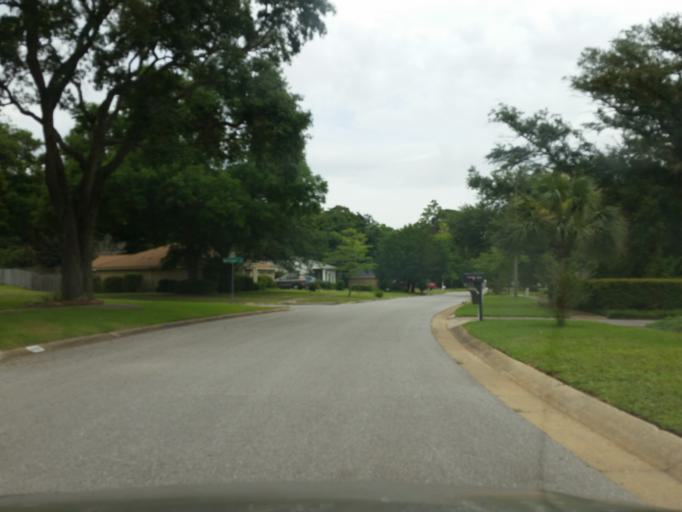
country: US
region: Florida
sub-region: Escambia County
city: Ferry Pass
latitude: 30.5204
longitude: -87.1811
